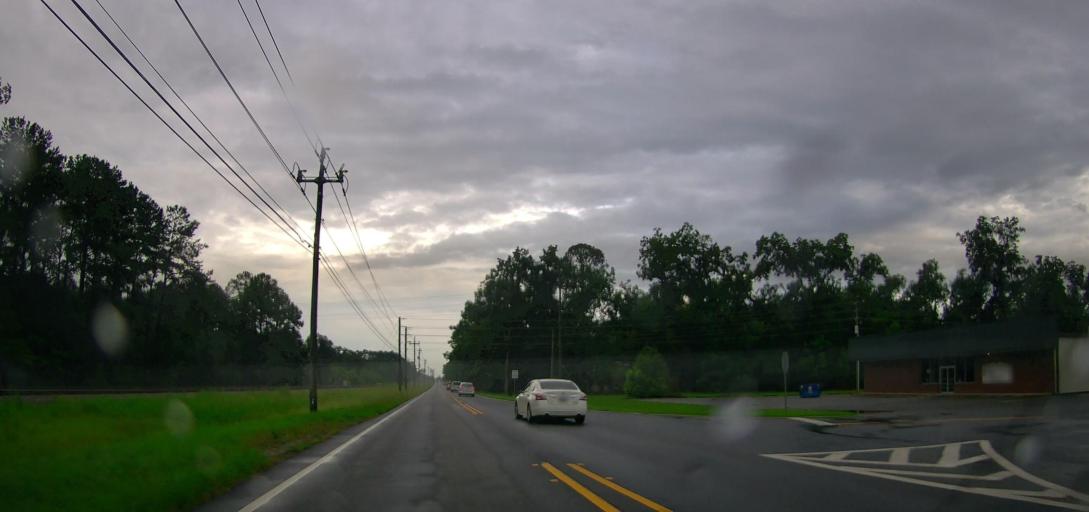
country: US
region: Georgia
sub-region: Ware County
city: Deenwood
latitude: 31.2465
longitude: -82.3742
